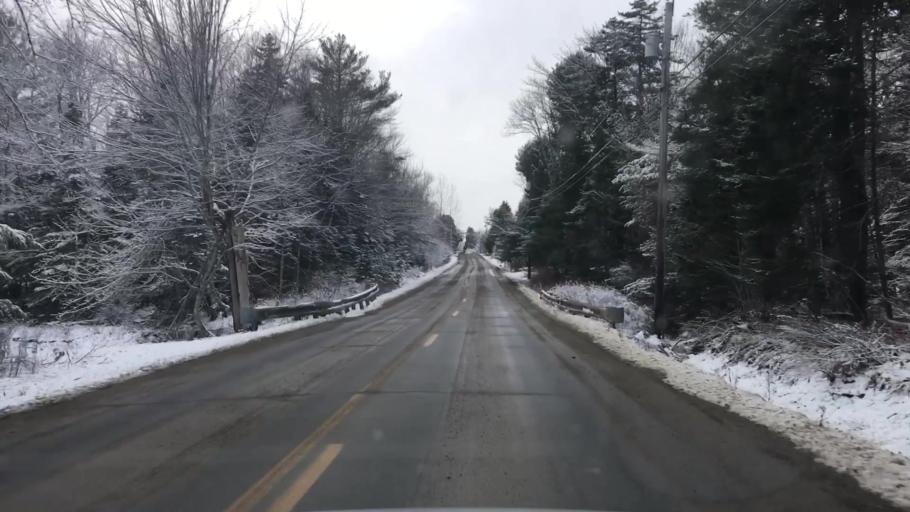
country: US
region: Maine
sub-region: Knox County
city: Owls Head
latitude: 44.0631
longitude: -69.0838
